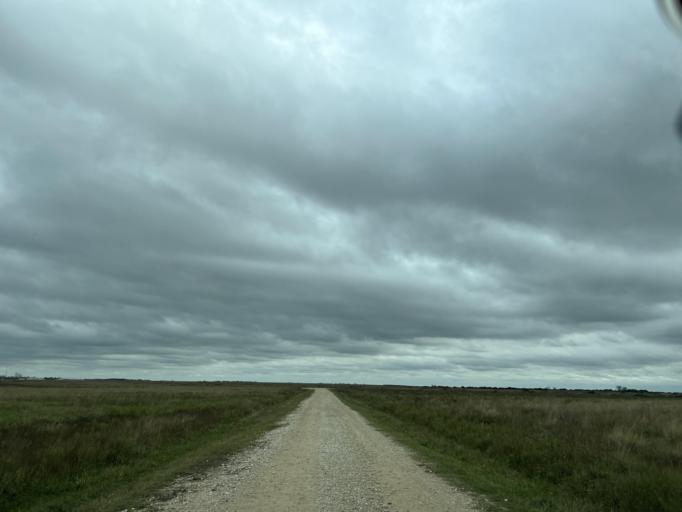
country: US
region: Texas
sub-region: Colorado County
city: Eagle Lake
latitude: 29.6668
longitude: -96.2814
